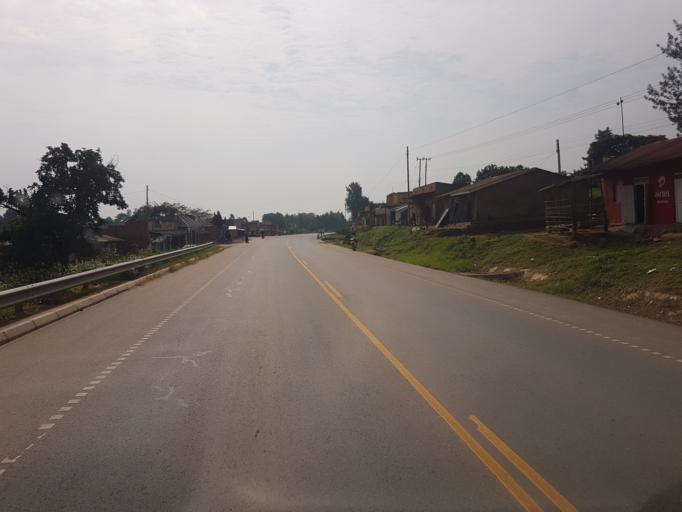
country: UG
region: Western Region
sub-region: Sheema District
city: Kibingo
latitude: -0.6358
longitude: 30.5187
